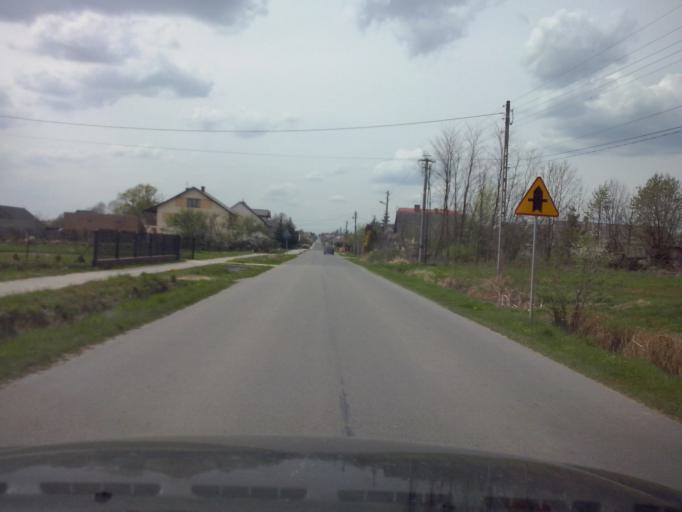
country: PL
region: Subcarpathian Voivodeship
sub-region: Powiat rzeszowski
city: Kamien
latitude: 50.3304
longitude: 22.1731
